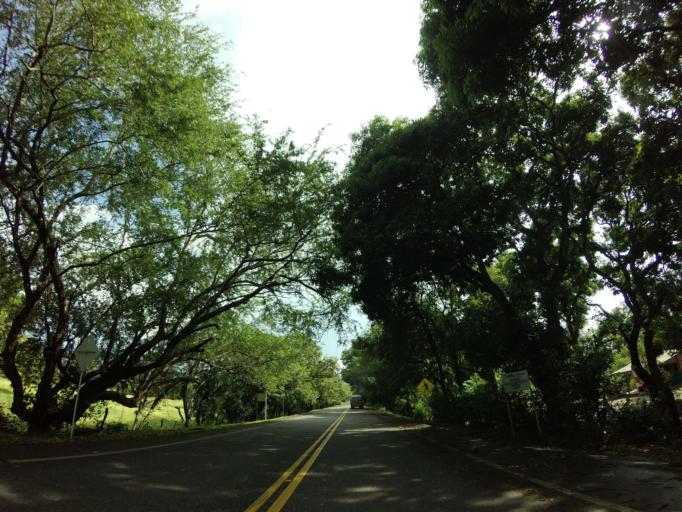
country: CO
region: Tolima
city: Honda
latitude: 5.3158
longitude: -74.7388
